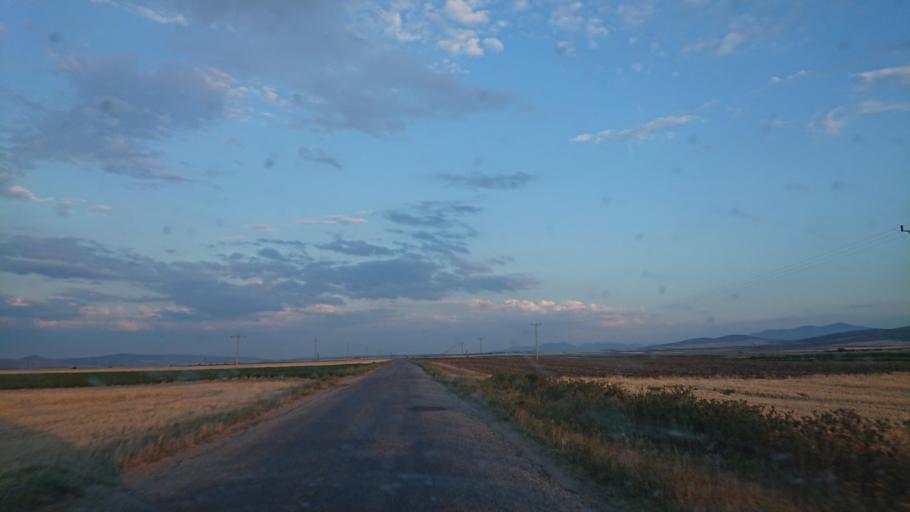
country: TR
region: Aksaray
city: Ortakoy
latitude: 38.8730
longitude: 34.0611
